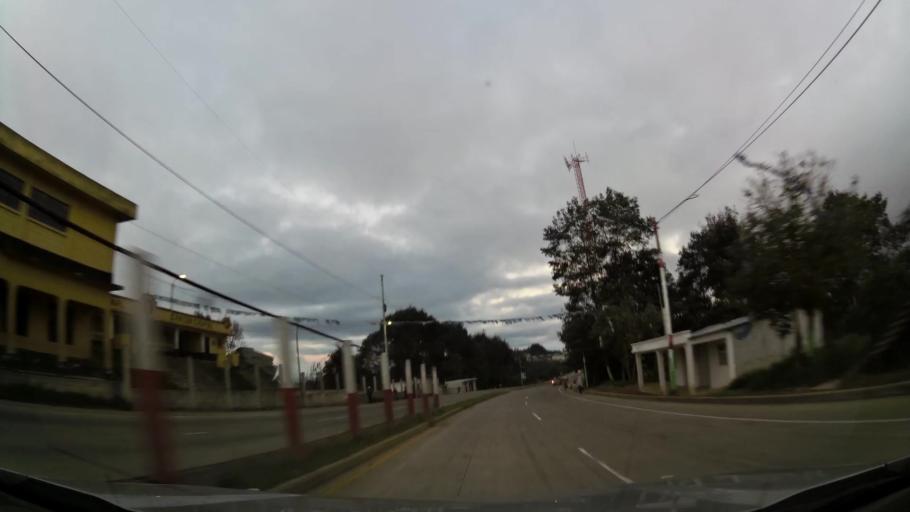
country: GT
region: Quiche
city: Chichicastenango
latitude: 14.8544
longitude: -91.0646
